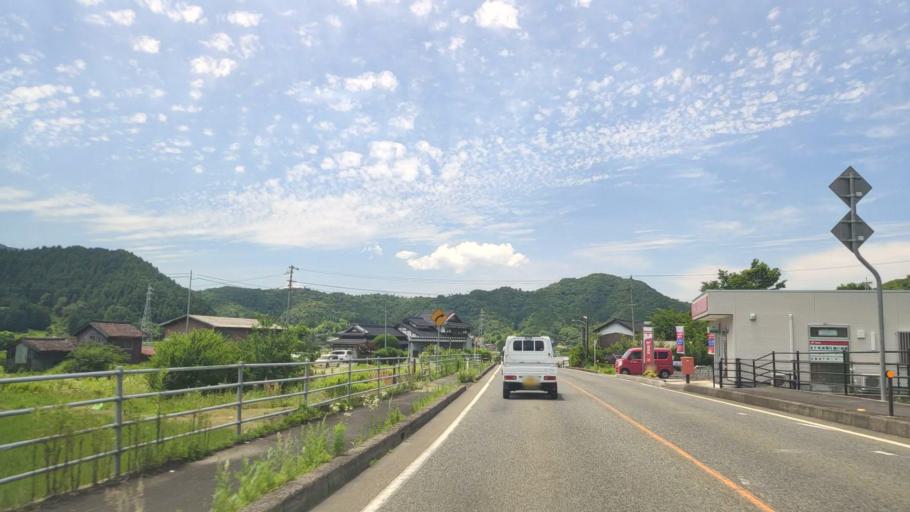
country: JP
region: Tottori
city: Tottori
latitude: 35.3754
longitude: 134.3018
